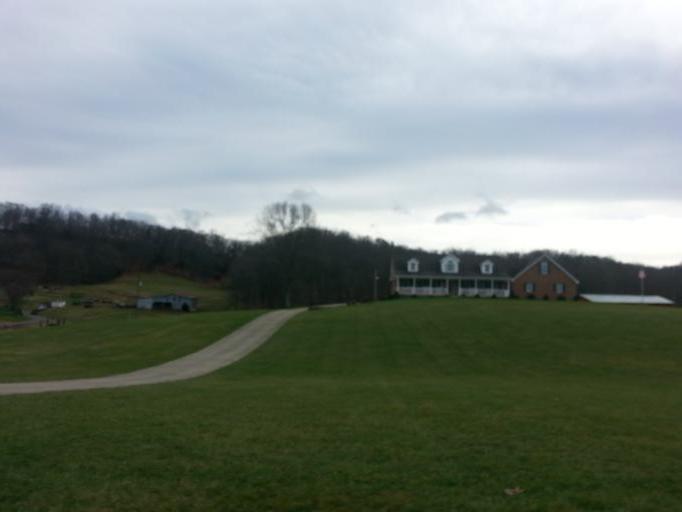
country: US
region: Tennessee
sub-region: Greene County
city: Greeneville
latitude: 36.1350
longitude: -82.8815
